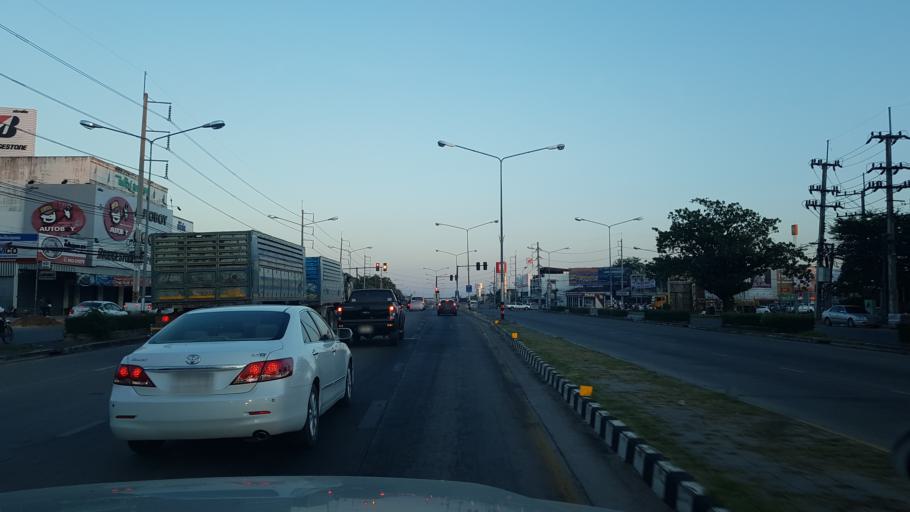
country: TH
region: Khon Kaen
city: Chum Phae
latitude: 16.5417
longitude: 102.1072
